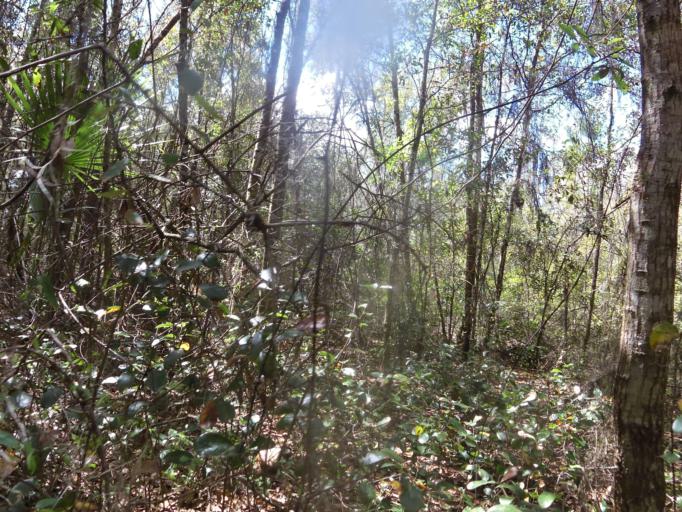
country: US
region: Florida
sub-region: Clay County
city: Keystone Heights
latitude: 29.7845
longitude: -81.8753
